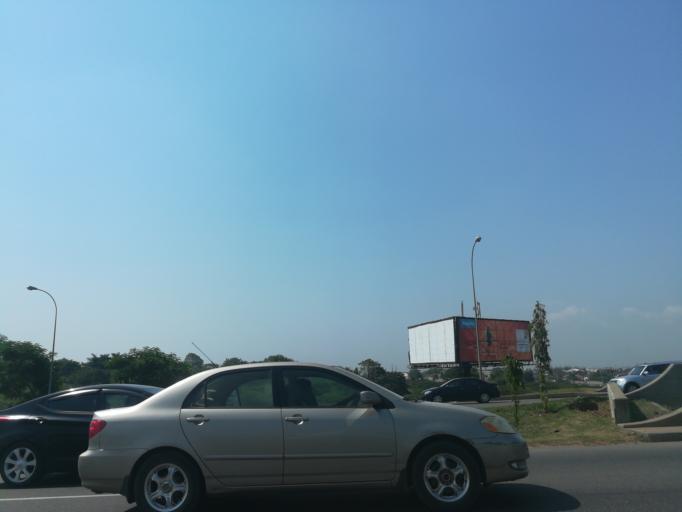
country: NG
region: Abuja Federal Capital Territory
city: Abuja
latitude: 9.0777
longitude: 7.4572
